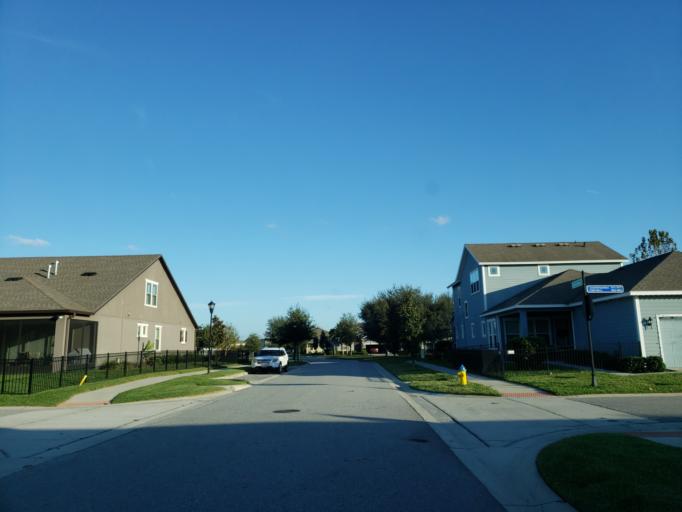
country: US
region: Florida
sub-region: Hillsborough County
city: Fish Hawk
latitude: 27.8500
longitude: -82.2519
